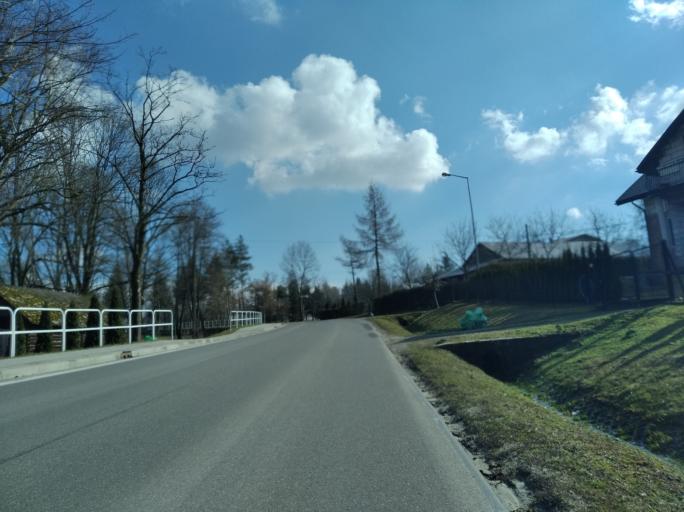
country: PL
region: Subcarpathian Voivodeship
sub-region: Powiat jasielski
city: Kolaczyce
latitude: 49.8511
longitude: 21.5161
